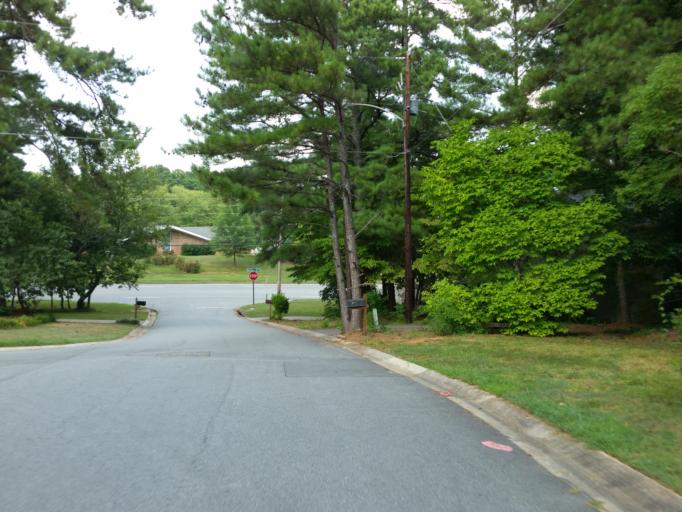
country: US
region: Georgia
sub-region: Fulton County
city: Roswell
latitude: 34.0361
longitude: -84.4475
